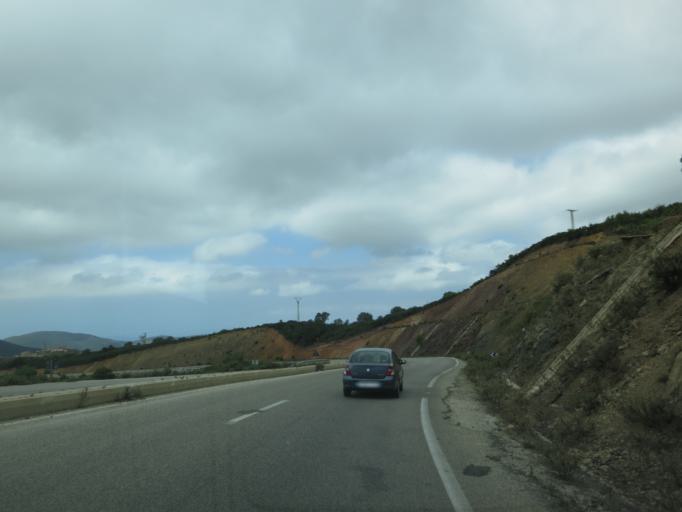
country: ES
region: Ceuta
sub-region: Ceuta
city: Ceuta
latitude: 35.8629
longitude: -5.4156
